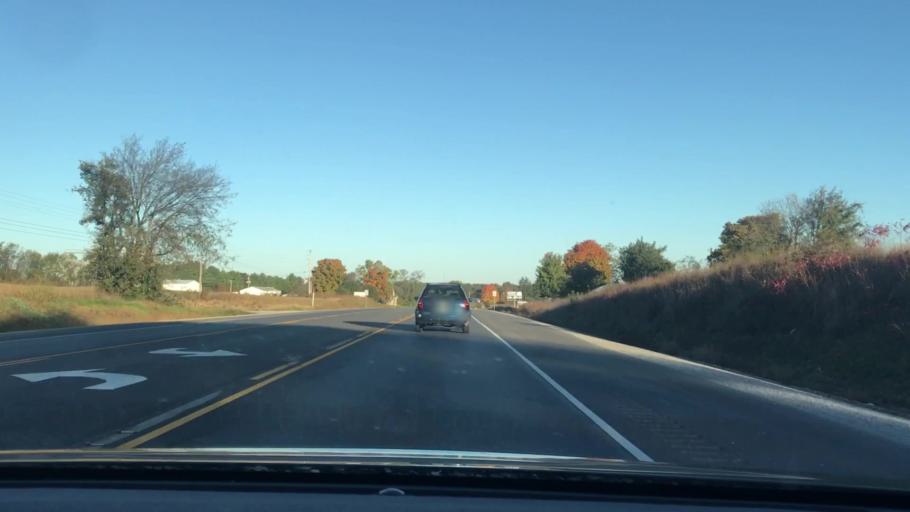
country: US
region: Kentucky
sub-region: Simpson County
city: Franklin
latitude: 36.6767
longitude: -86.5627
